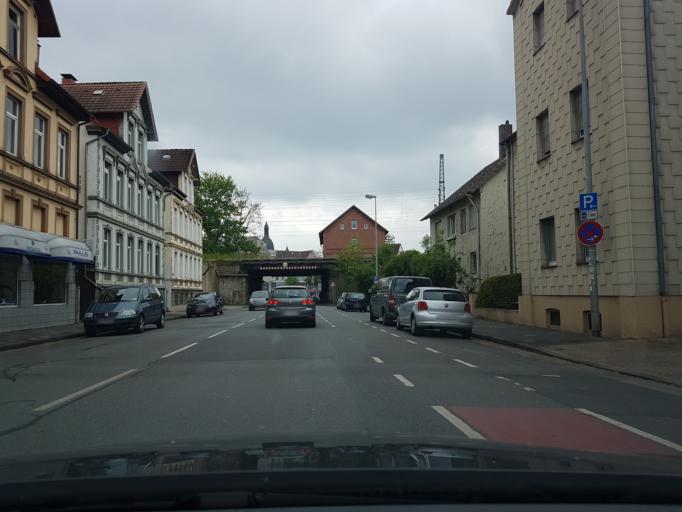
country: DE
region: Lower Saxony
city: Hameln
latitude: 52.1031
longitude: 9.3736
